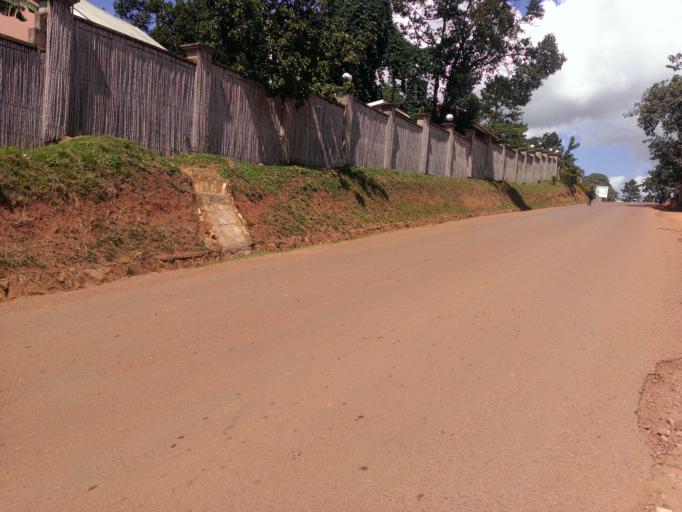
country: UG
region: Central Region
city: Kampala Central Division
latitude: 0.3303
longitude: 32.5536
